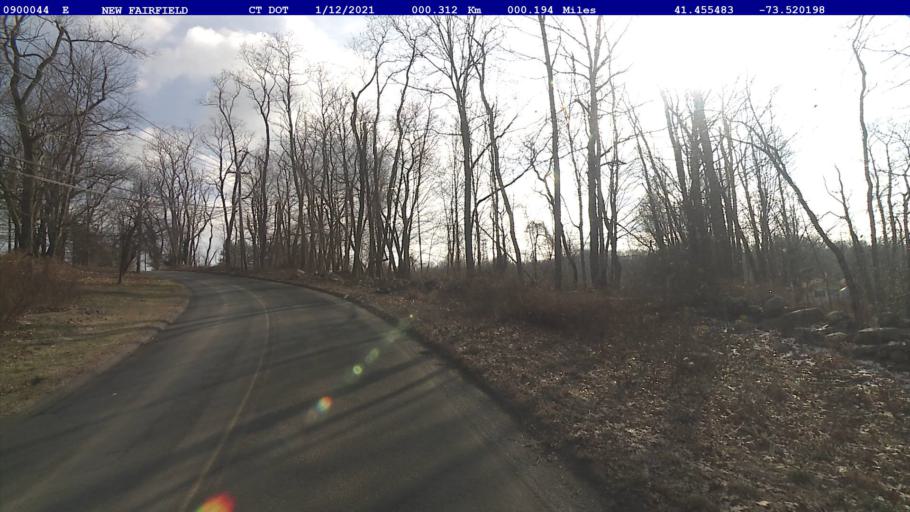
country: US
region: New York
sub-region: Putnam County
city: Putnam Lake
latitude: 41.4555
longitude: -73.5202
